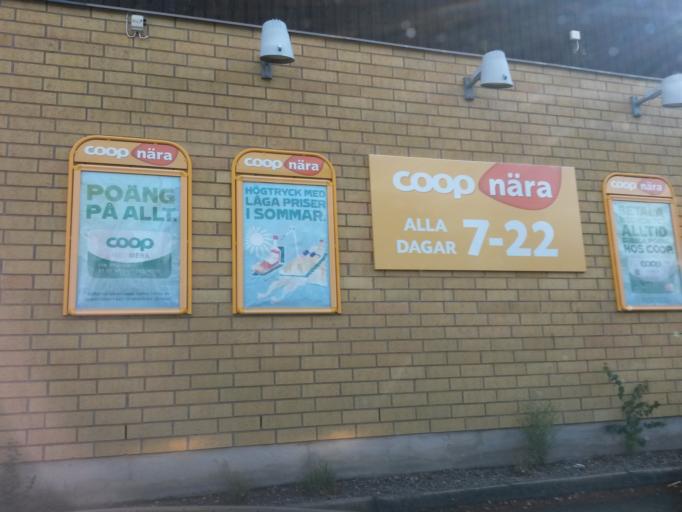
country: SE
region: Joenkoeping
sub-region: Varnamo Kommun
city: Bor
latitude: 57.1152
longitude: 14.1683
